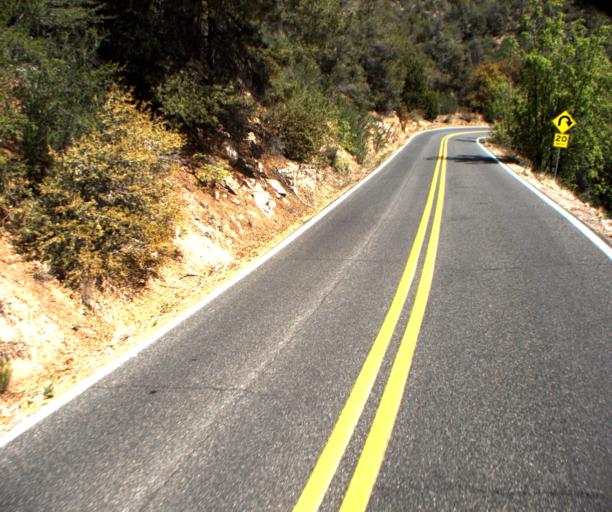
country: US
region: Arizona
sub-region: Yavapai County
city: Clarkdale
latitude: 34.7414
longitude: -112.1400
